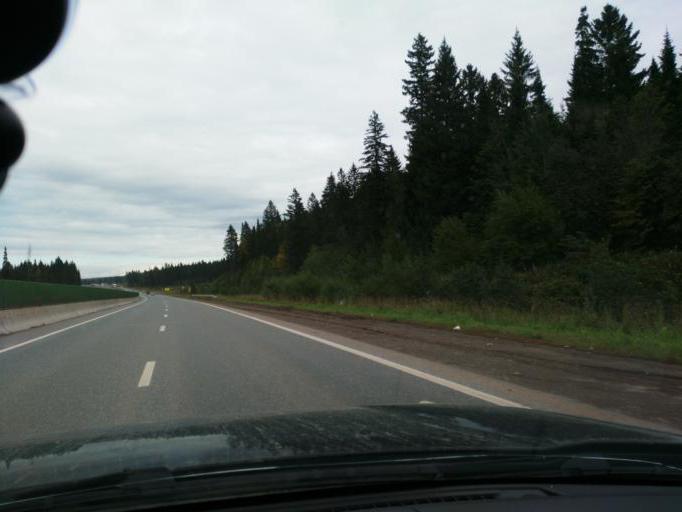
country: RU
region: Perm
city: Ferma
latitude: 57.9429
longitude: 56.3783
